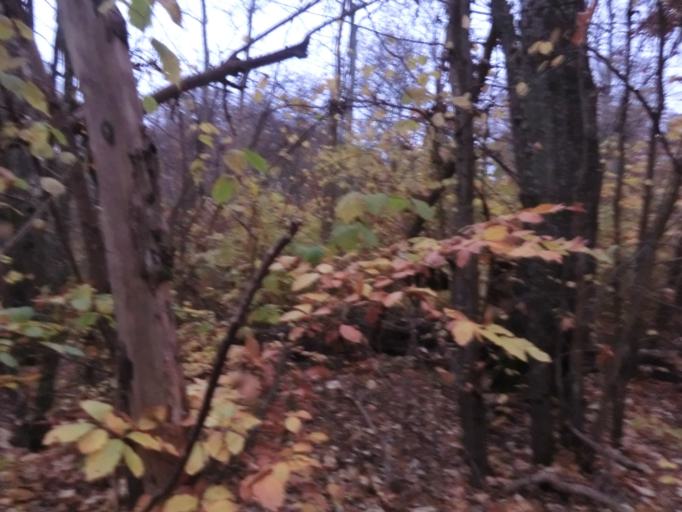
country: SE
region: Skane
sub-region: Lunds Kommun
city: Genarp
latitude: 55.6746
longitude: 13.3358
